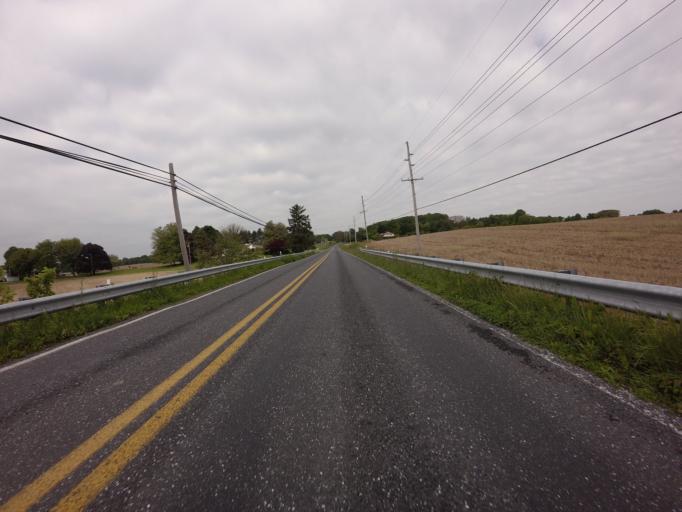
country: US
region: Maryland
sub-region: Frederick County
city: Green Valley
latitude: 39.2863
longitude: -77.2738
